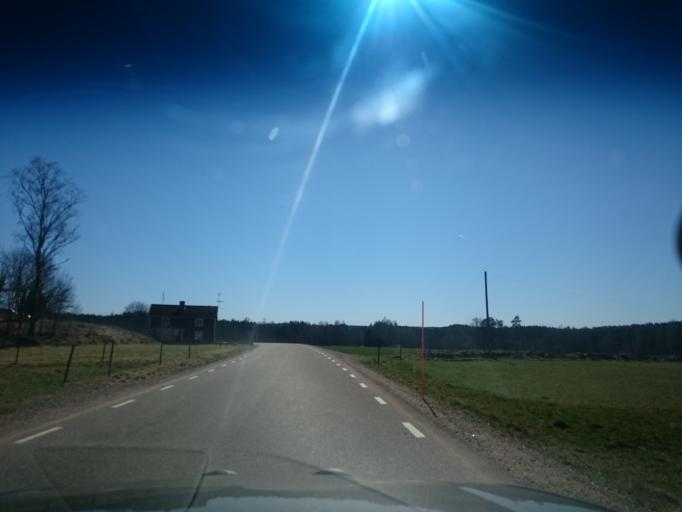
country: SE
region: Joenkoeping
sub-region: Vetlanda Kommun
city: Landsbro
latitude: 57.2217
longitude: 14.9547
